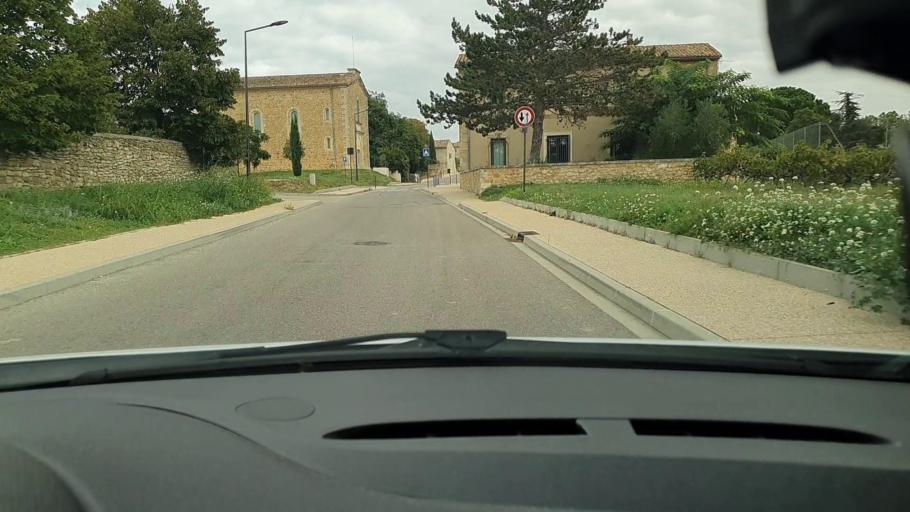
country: FR
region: Languedoc-Roussillon
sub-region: Departement du Gard
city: Saint-Chaptes
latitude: 44.0411
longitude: 4.2982
